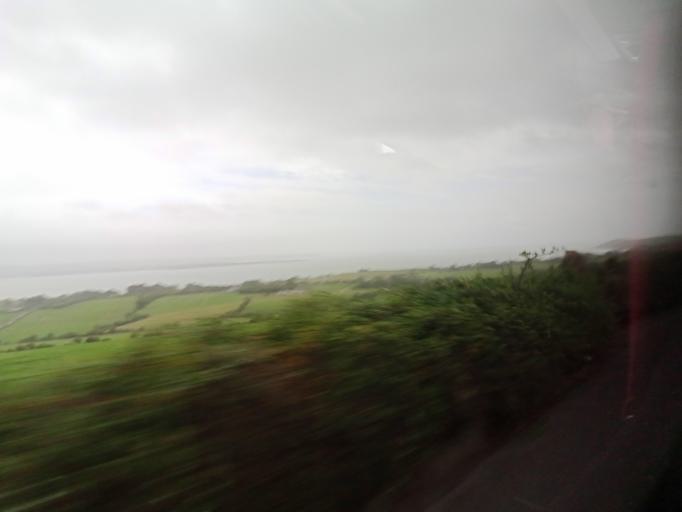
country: IE
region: Munster
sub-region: Waterford
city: Dungarvan
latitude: 52.0499
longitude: -7.6144
